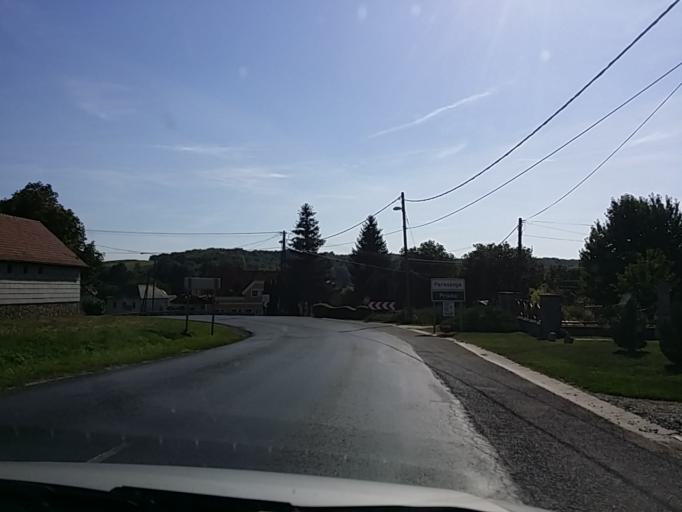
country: AT
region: Burgenland
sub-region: Politischer Bezirk Oberpullendorf
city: Lutzmannsburg
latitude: 47.4276
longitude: 16.6501
